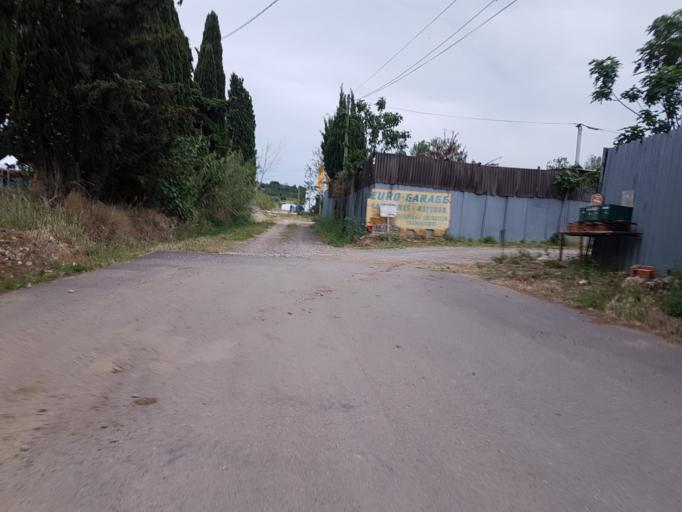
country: FR
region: Languedoc-Roussillon
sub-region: Departement de l'Herault
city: Portiragnes
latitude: 43.3144
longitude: 3.3436
